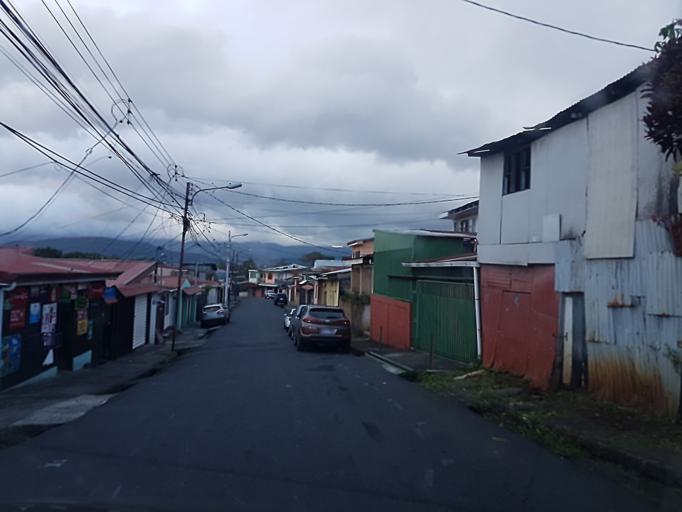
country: CR
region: San Jose
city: San Pedro
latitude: 9.9276
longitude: -84.0461
